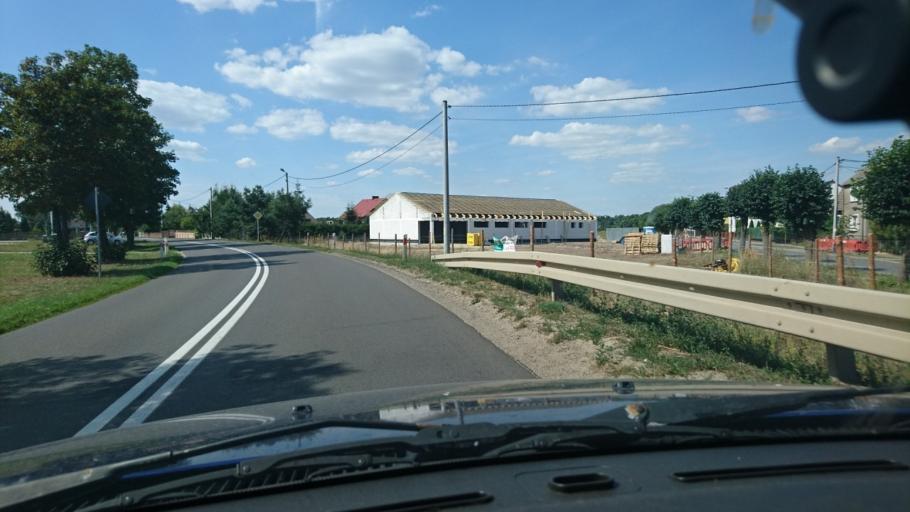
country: PL
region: Greater Poland Voivodeship
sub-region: Powiat krotoszynski
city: Sulmierzyce
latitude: 51.6140
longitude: 17.5144
